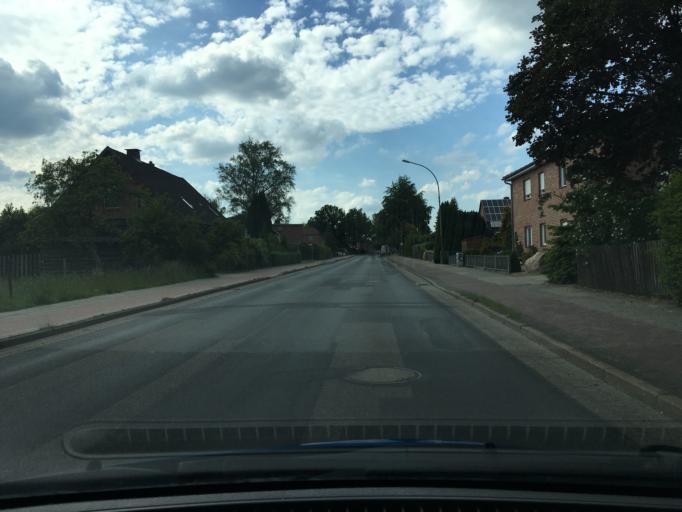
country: DE
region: Lower Saxony
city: Tostedt
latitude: 53.2710
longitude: 9.7229
